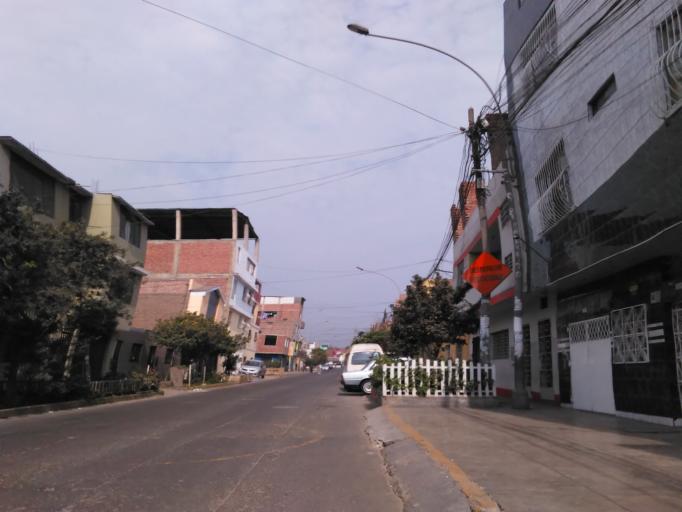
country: PE
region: Callao
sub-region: Callao
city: Callao
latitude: -12.0375
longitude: -77.0792
